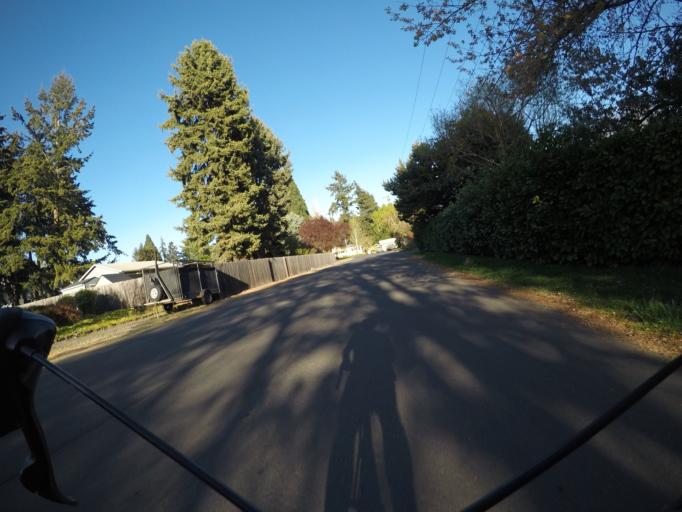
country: US
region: Oregon
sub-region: Washington County
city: Aloha
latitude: 45.4851
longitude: -122.8748
